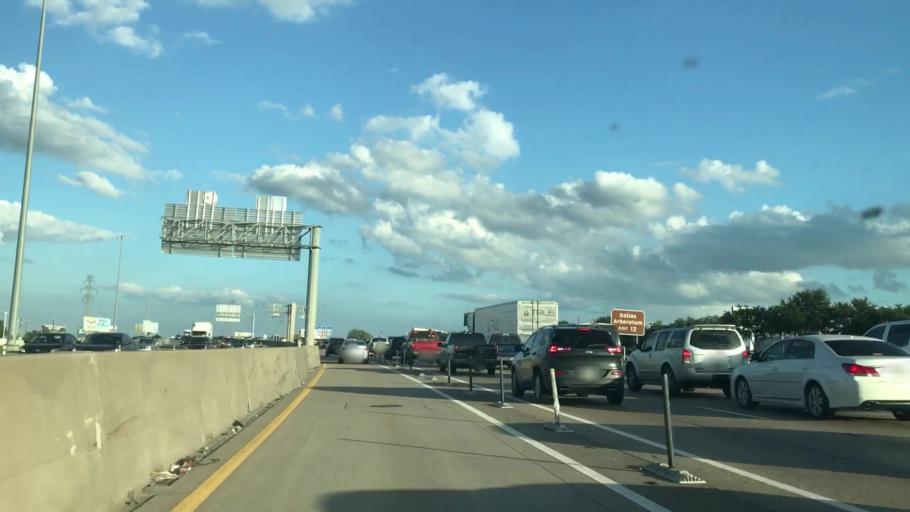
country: US
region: Texas
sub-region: Dallas County
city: Garland
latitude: 32.8722
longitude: -96.6796
